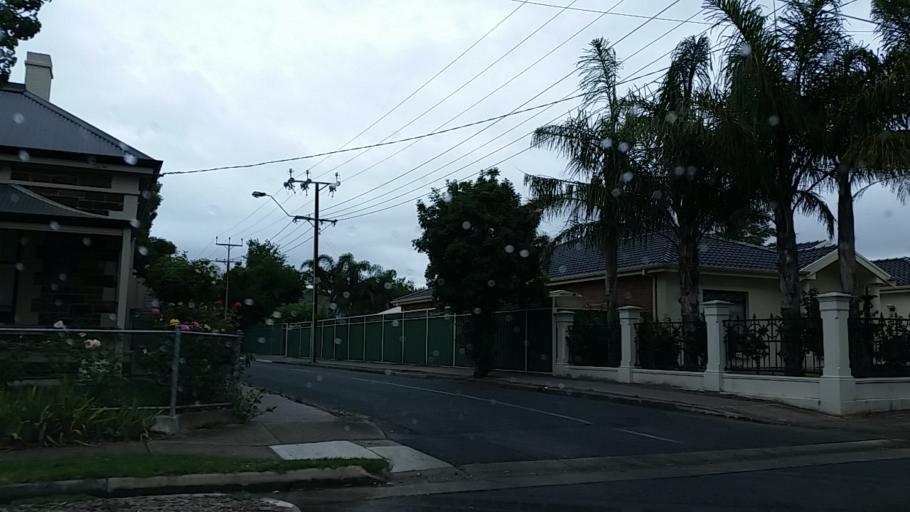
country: AU
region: South Australia
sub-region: Prospect
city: Prospect
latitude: -34.8789
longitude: 138.5979
